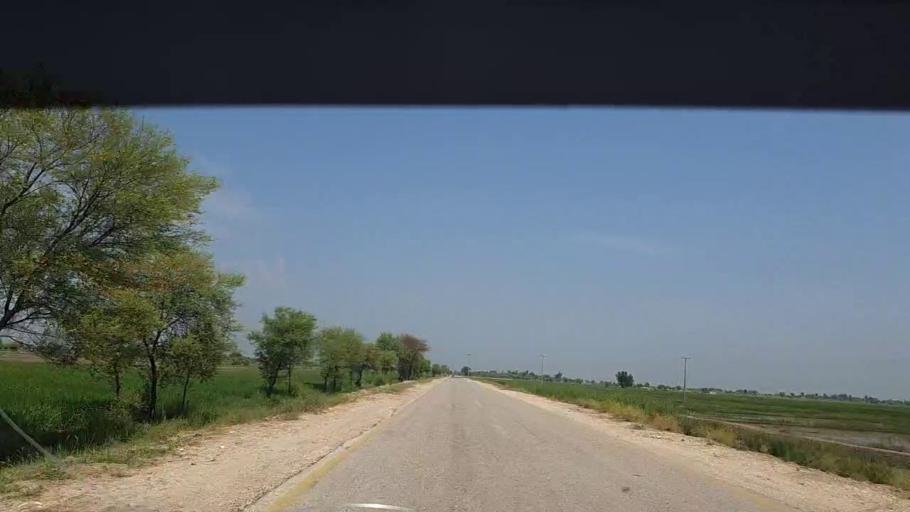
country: PK
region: Sindh
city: Rustam jo Goth
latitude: 28.1005
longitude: 68.8027
